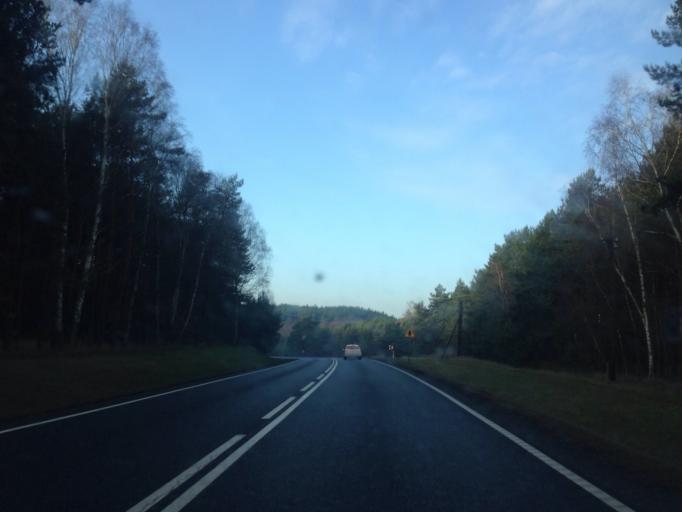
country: PL
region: Kujawsko-Pomorskie
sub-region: Powiat torunski
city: Wielka Nieszawka
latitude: 52.9987
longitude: 18.4617
